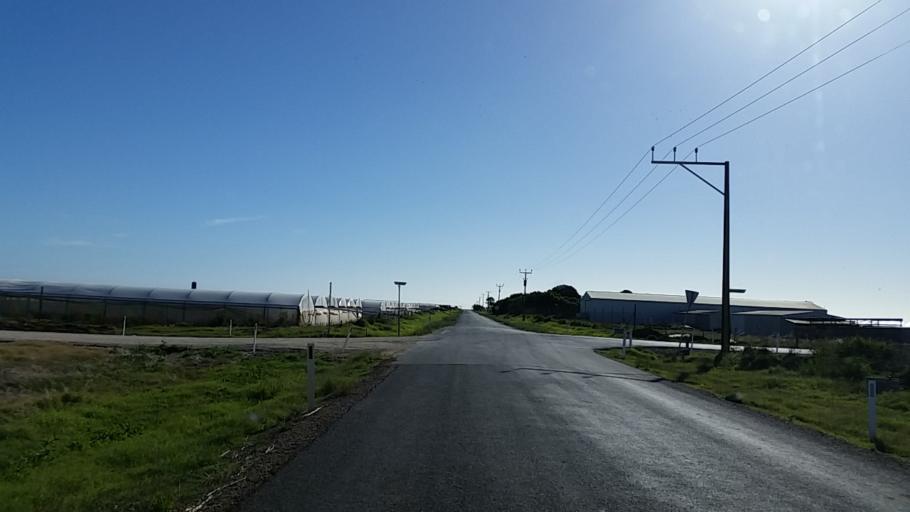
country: AU
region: South Australia
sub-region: Playford
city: Virginia
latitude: -34.6769
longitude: 138.5378
